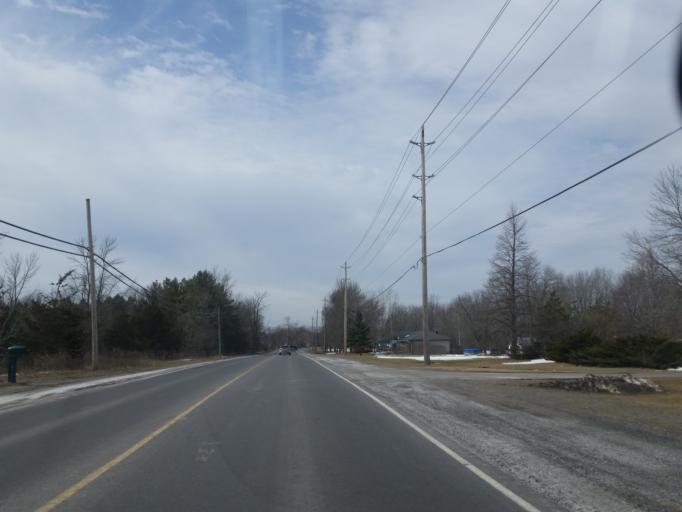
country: CA
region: Ontario
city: Belleville
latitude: 44.1757
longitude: -77.2950
